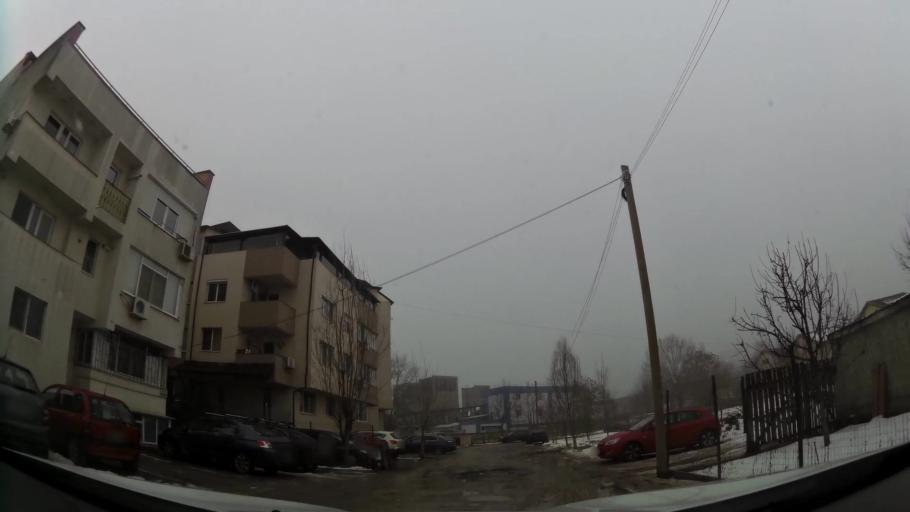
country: RO
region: Ilfov
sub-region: Comuna Chiajna
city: Rosu
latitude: 44.4385
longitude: 25.9984
